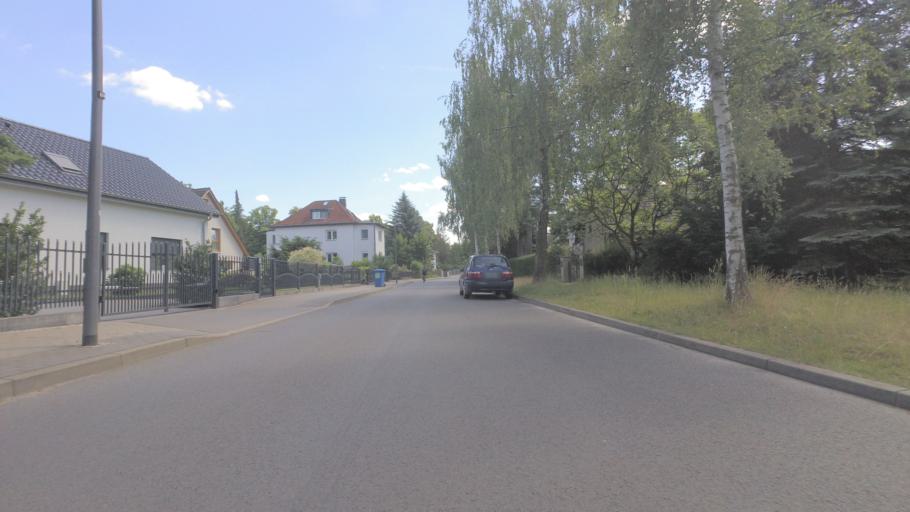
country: DE
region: Brandenburg
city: Rangsdorf
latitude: 52.2883
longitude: 13.4180
